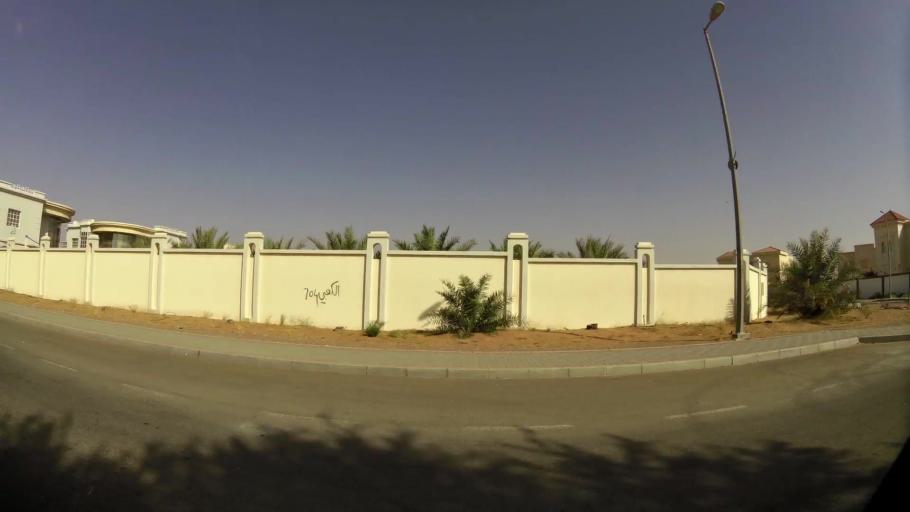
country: OM
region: Al Buraimi
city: Al Buraymi
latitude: 24.3499
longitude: 55.7974
